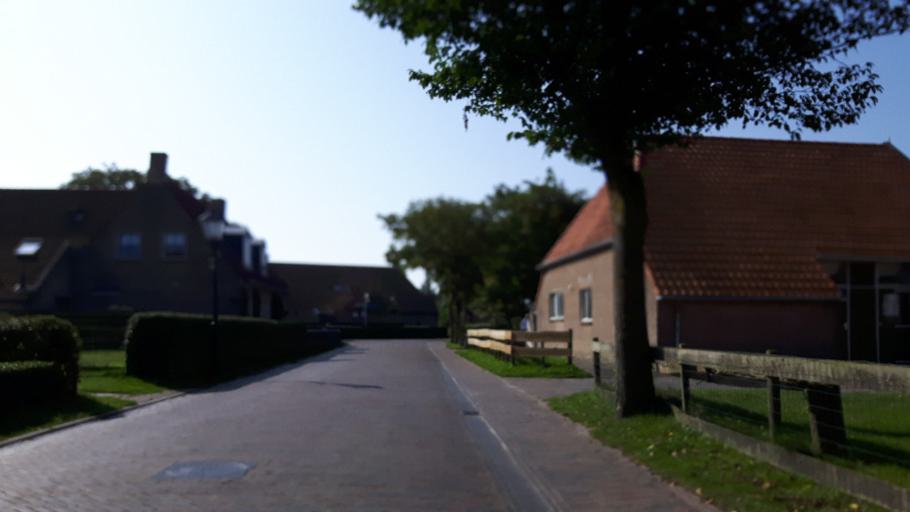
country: NL
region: Friesland
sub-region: Gemeente Ameland
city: Nes
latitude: 53.4483
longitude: 5.7998
